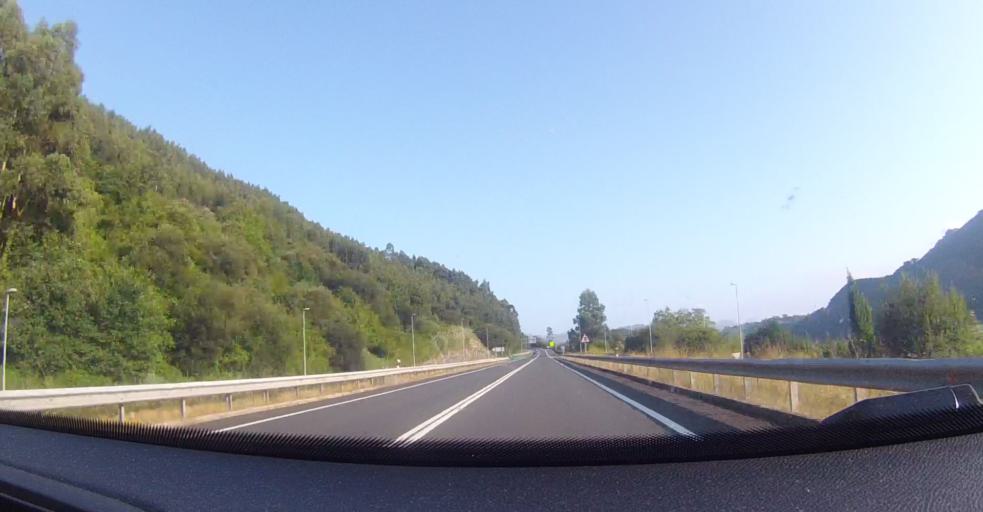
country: ES
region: Cantabria
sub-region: Provincia de Cantabria
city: Limpias
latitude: 43.3735
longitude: -3.4289
